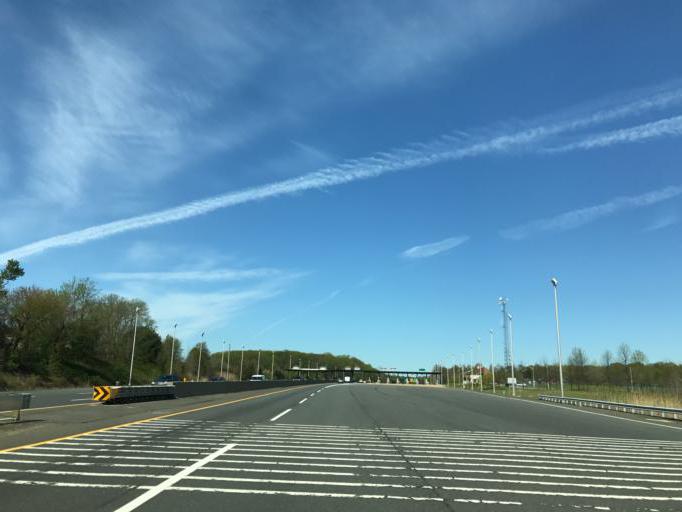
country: US
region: New Jersey
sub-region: Burlington County
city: Roebling
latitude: 40.0959
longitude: -74.7739
